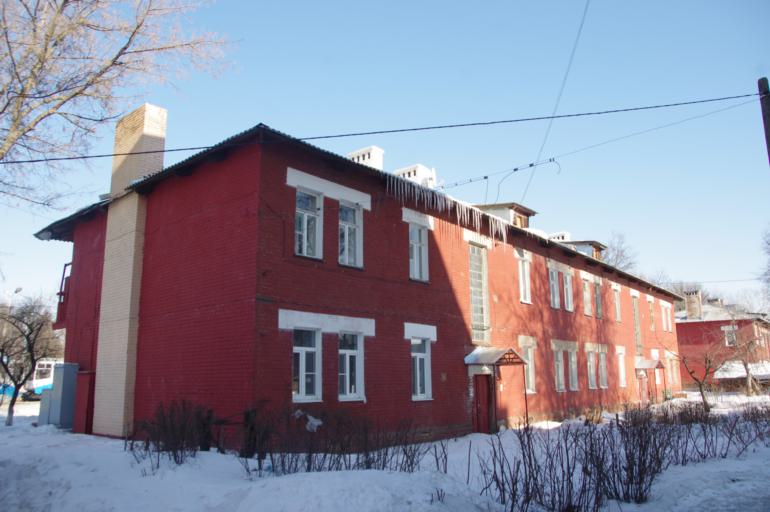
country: RU
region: Moskovskaya
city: Kolomna
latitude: 55.0933
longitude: 38.7690
